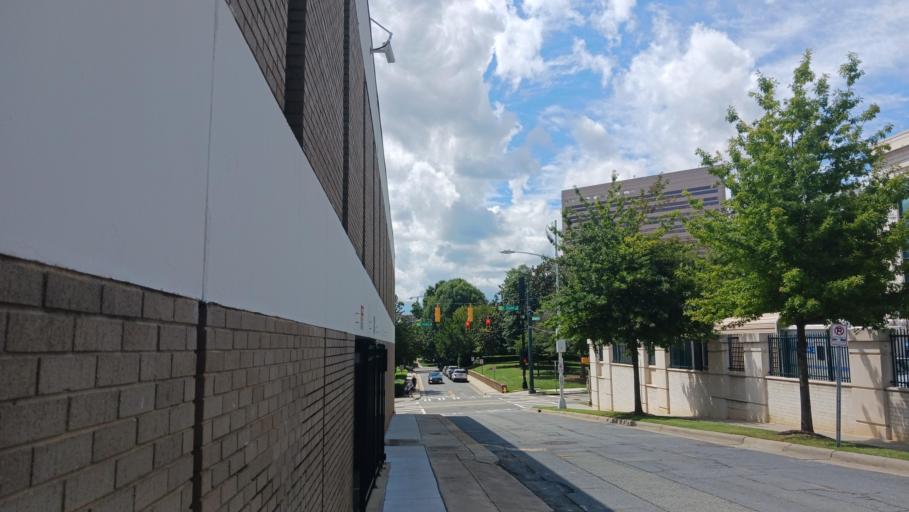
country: US
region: North Carolina
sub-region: Mecklenburg County
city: Charlotte
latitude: 35.2225
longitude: -80.8365
